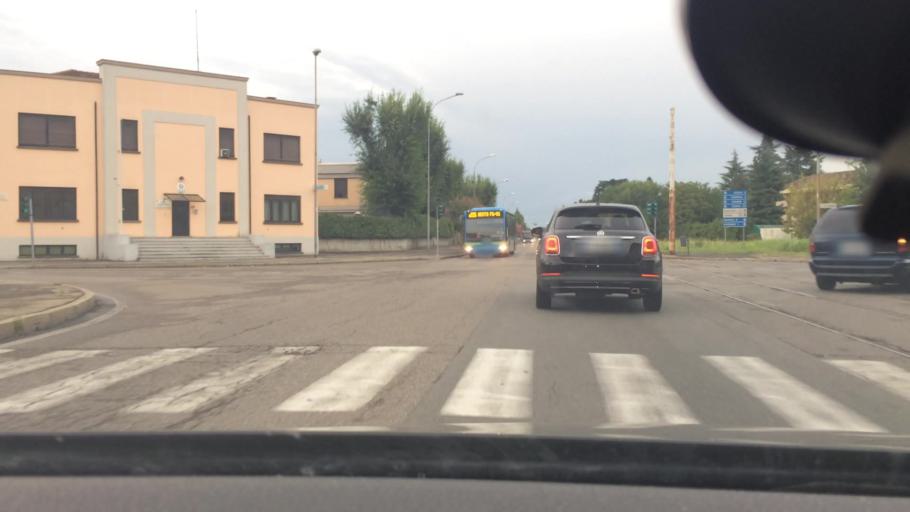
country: IT
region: Lombardy
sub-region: Provincia di Monza e Brianza
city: Nova Milanese
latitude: 45.5918
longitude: 9.1979
